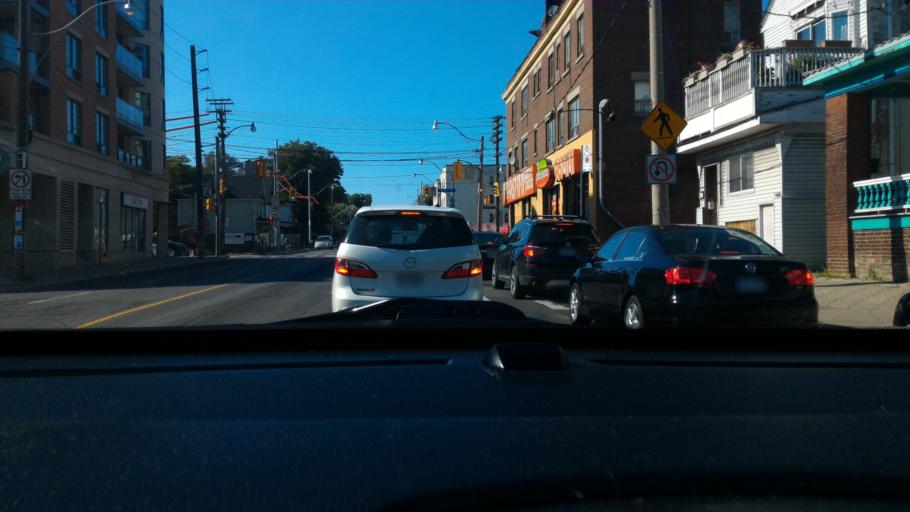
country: CA
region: Ontario
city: Scarborough
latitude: 43.6682
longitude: -79.3056
